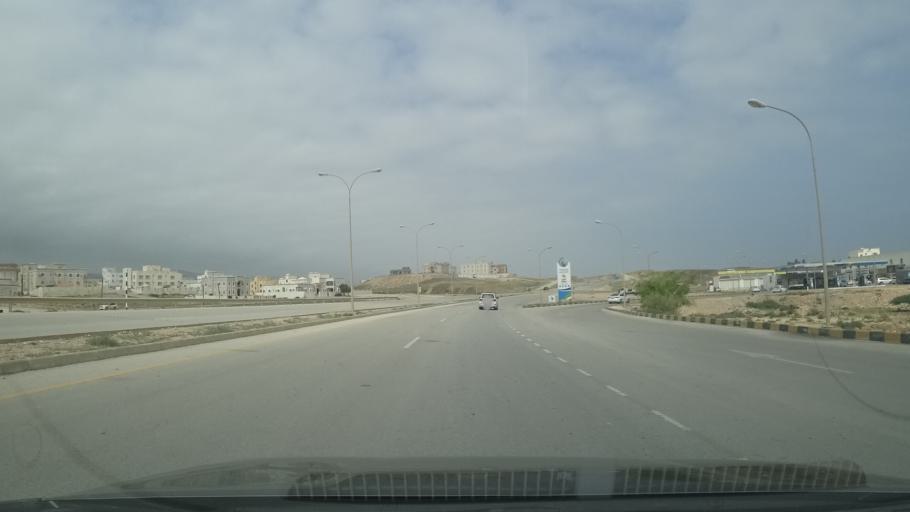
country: OM
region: Zufar
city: Salalah
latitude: 17.0507
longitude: 54.3895
